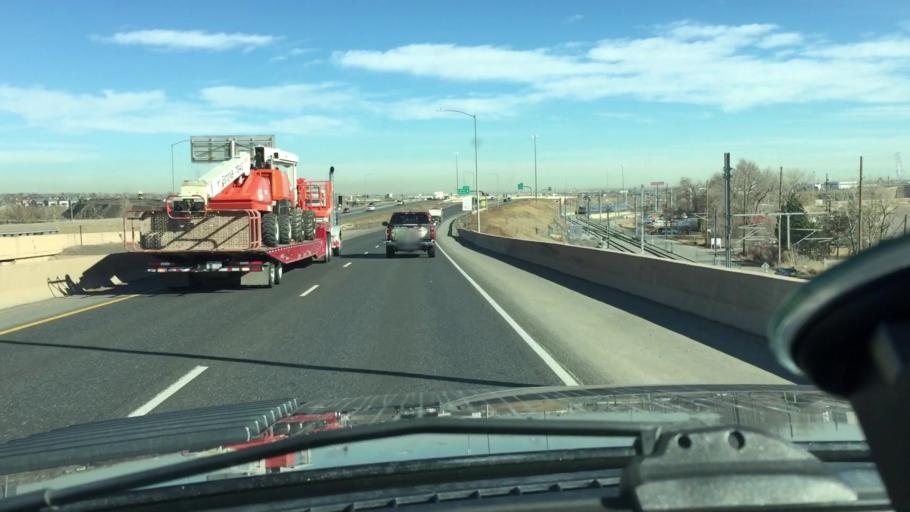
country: US
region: Colorado
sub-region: Adams County
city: Berkley
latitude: 39.8053
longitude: -105.0150
